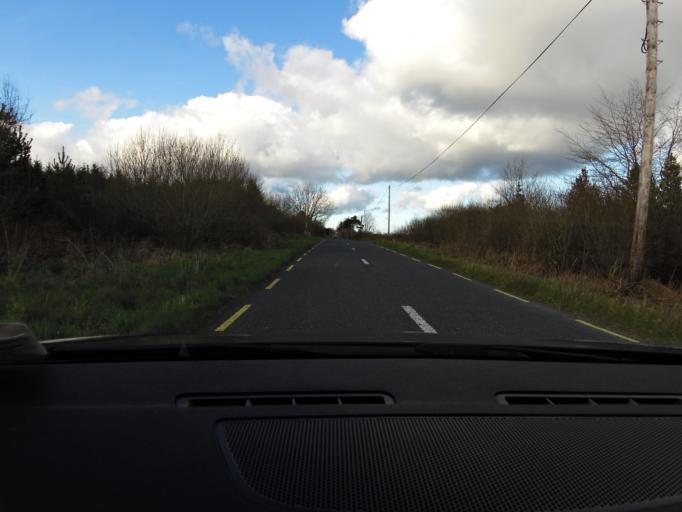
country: IE
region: Connaught
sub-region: Roscommon
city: Castlerea
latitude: 53.6639
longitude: -8.5048
